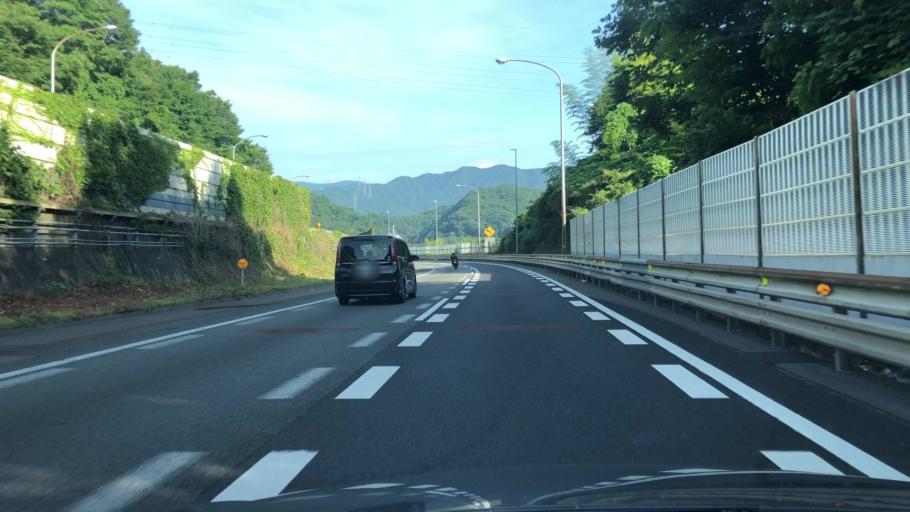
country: JP
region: Shizuoka
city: Gotemba
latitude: 35.3561
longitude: 139.0027
